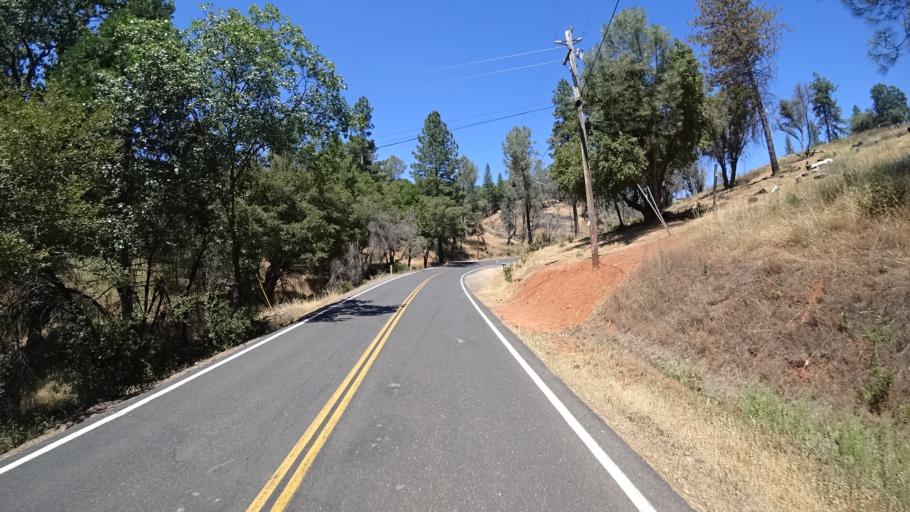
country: US
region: California
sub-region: Calaveras County
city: Mountain Ranch
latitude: 38.2783
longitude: -120.5069
